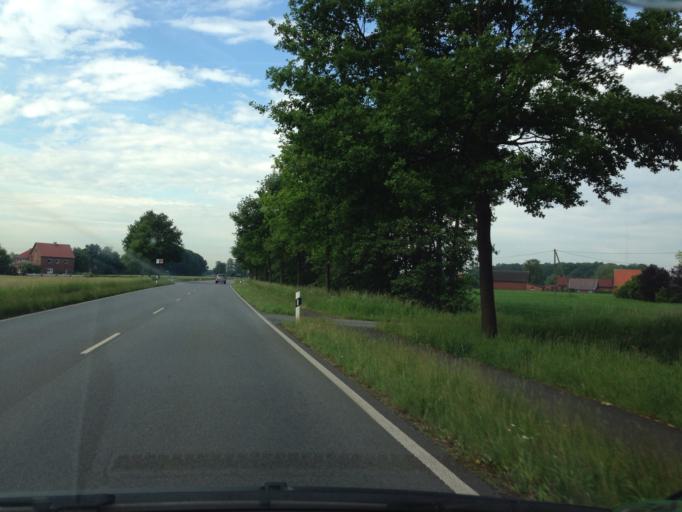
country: DE
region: North Rhine-Westphalia
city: Ludinghausen
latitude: 51.7942
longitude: 7.4704
